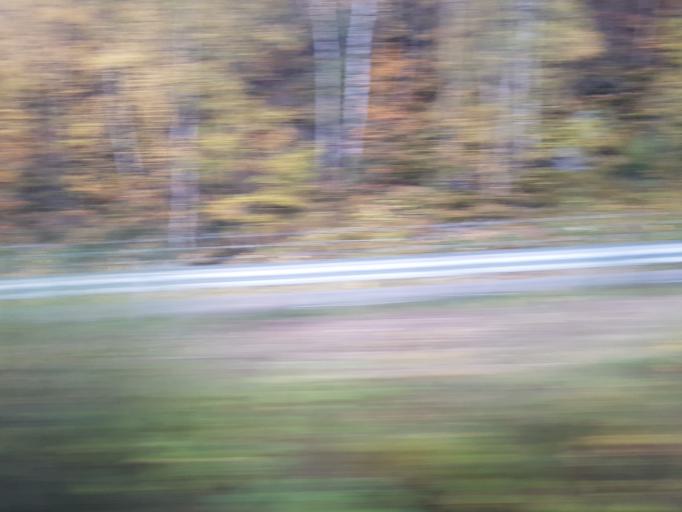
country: NO
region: Oppland
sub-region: Sel
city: Otta
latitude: 61.8373
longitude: 9.4800
